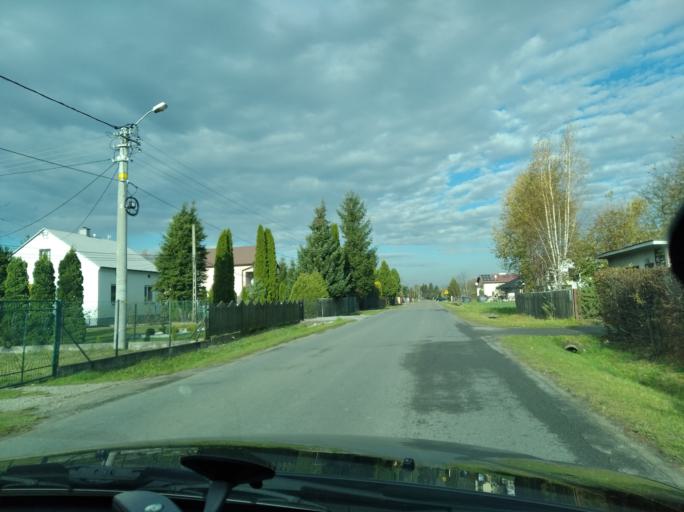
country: PL
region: Subcarpathian Voivodeship
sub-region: Powiat debicki
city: Brzeznica
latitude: 50.0751
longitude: 21.5265
